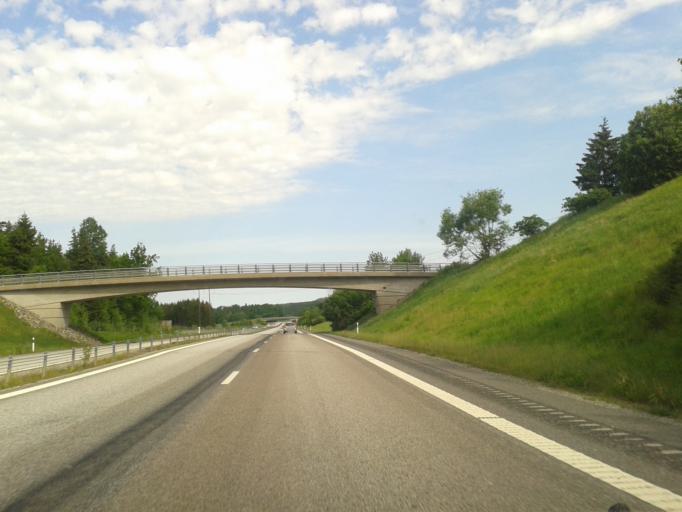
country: SE
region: Vaestra Goetaland
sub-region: Munkedals Kommun
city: Munkedal
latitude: 58.5307
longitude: 11.5390
